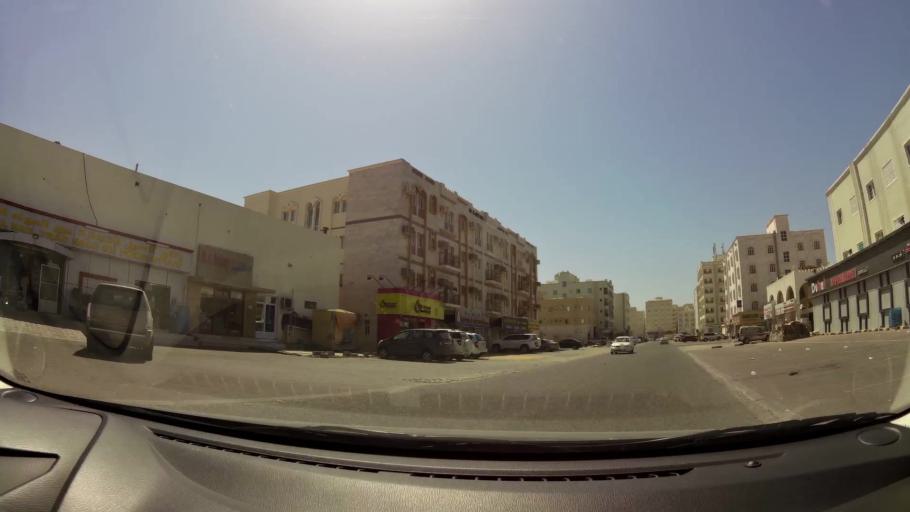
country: OM
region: Muhafazat Masqat
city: As Sib al Jadidah
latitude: 23.6243
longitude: 58.2200
